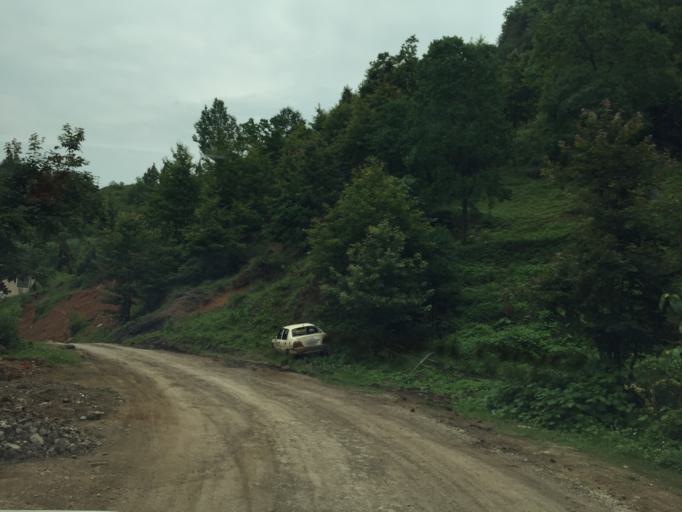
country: CN
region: Guizhou Sheng
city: Tongjing
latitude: 28.3704
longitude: 108.2394
